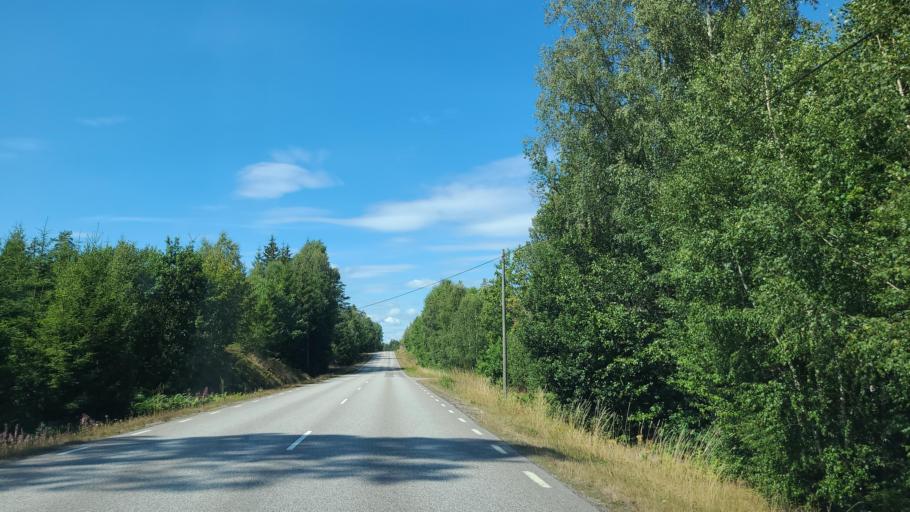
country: SE
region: Kalmar
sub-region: Nybro Kommun
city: Nybro
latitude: 56.5617
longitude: 15.7696
